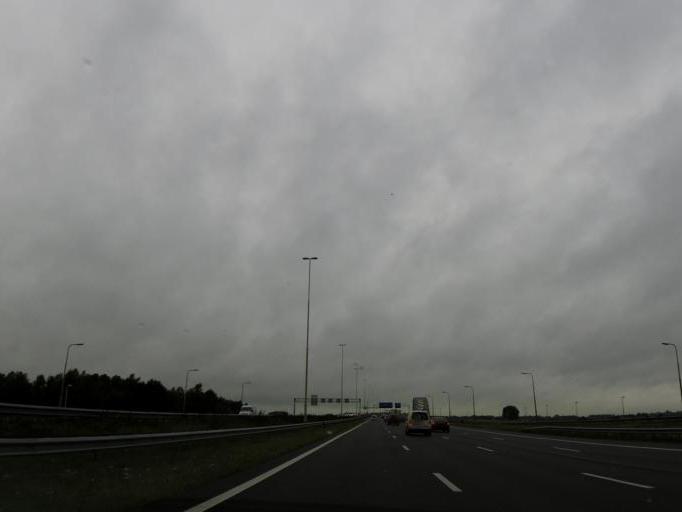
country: NL
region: Utrecht
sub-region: Gemeente Vianen
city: Vianen
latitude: 51.9912
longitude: 5.0815
